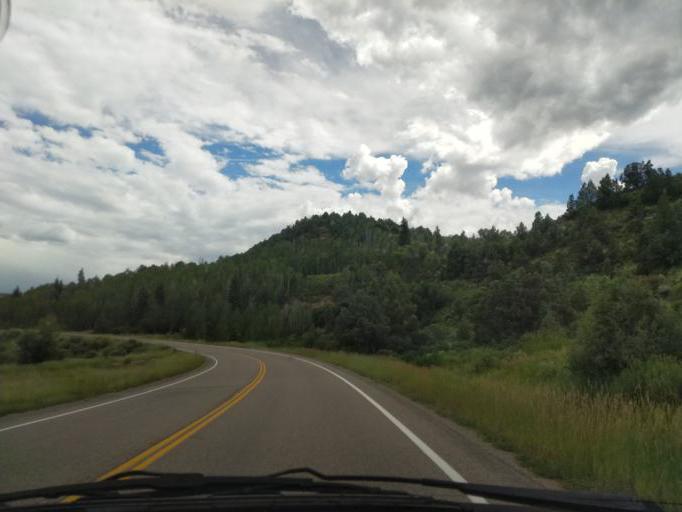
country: US
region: Colorado
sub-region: Delta County
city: Paonia
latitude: 39.0721
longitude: -107.3690
